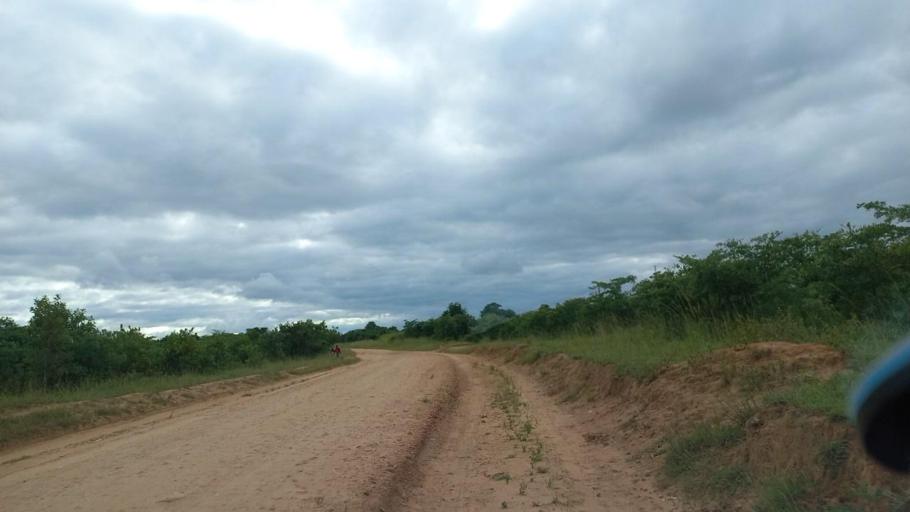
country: ZM
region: Lusaka
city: Chongwe
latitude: -15.4492
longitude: 28.8409
